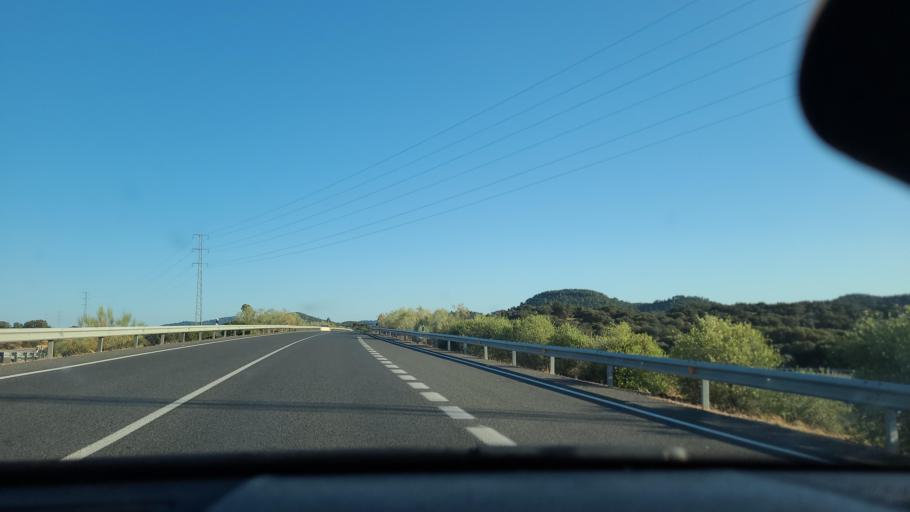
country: ES
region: Andalusia
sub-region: Province of Cordoba
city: Obejo
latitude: 38.0503
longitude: -4.8094
